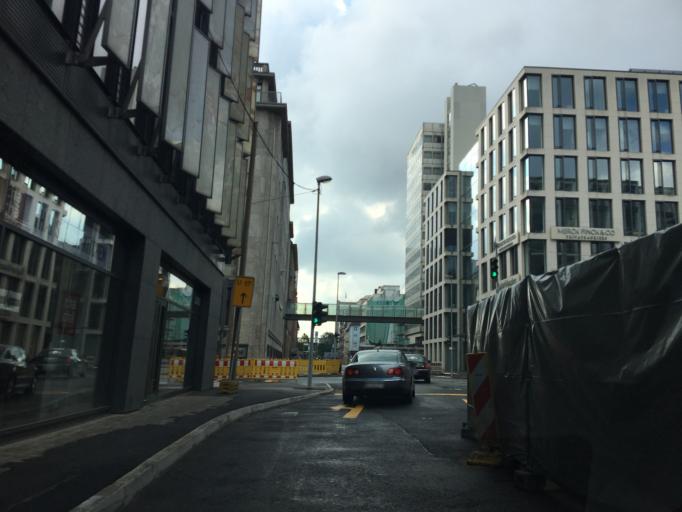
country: DE
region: North Rhine-Westphalia
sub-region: Regierungsbezirk Dusseldorf
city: Dusseldorf
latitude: 51.2234
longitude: 6.7757
